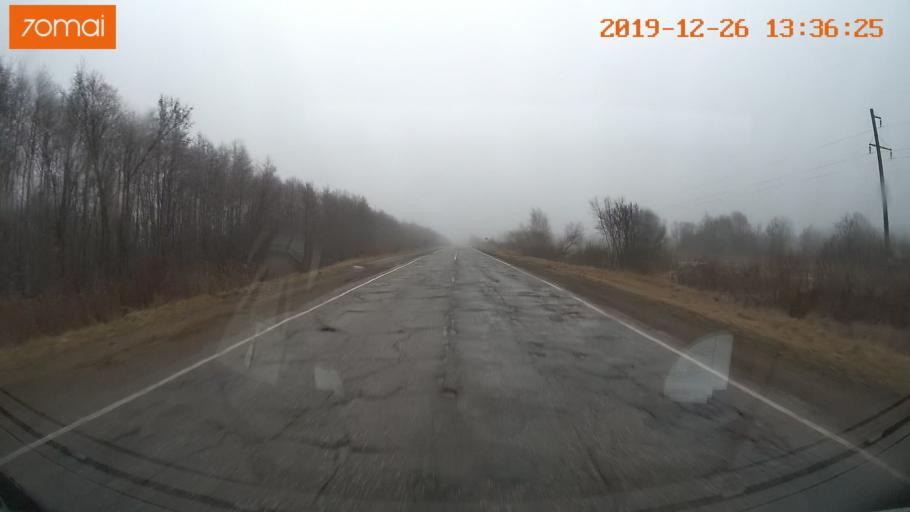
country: RU
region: Vologda
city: Sheksna
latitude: 58.7828
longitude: 38.3551
